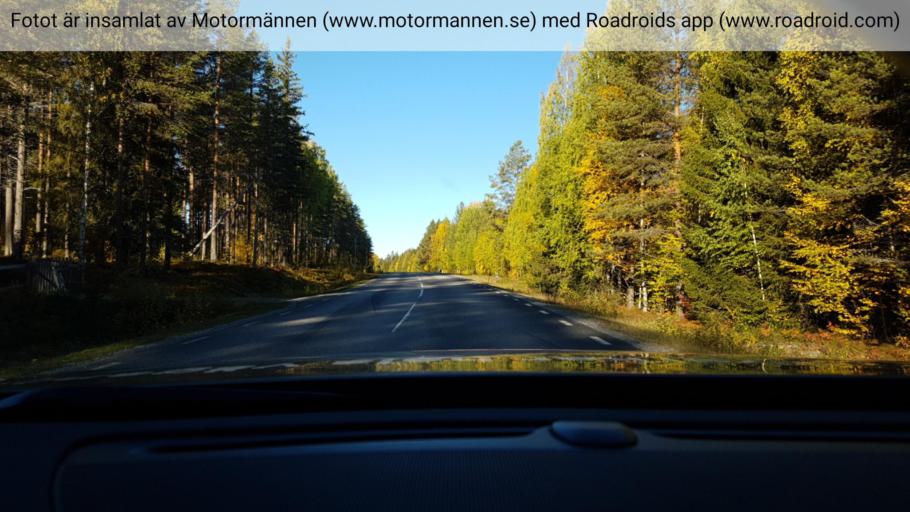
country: SE
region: Norrbotten
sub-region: Pitea Kommun
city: Roknas
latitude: 65.3567
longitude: 21.0777
